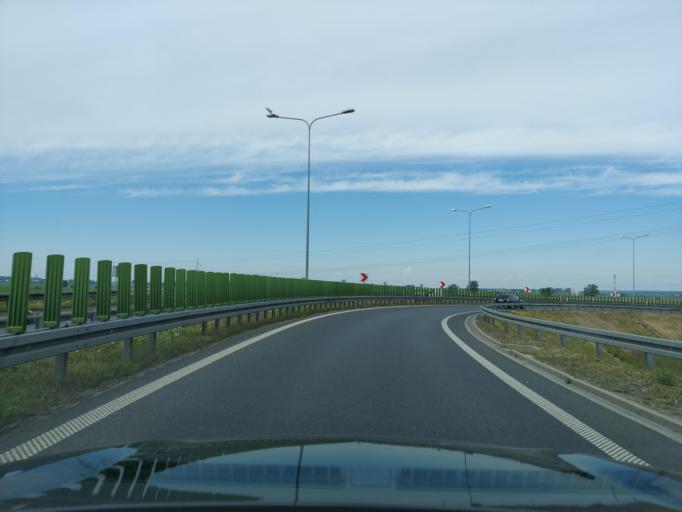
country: PL
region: Greater Poland Voivodeship
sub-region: Powiat poznanski
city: Komorniki
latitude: 52.3459
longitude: 16.7546
